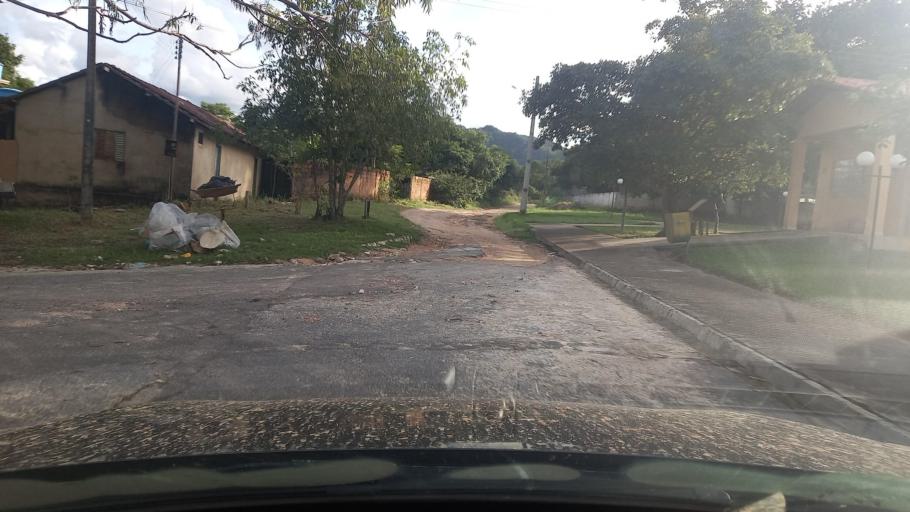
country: BR
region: Goias
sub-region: Cavalcante
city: Cavalcante
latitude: -13.7970
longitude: -47.4625
